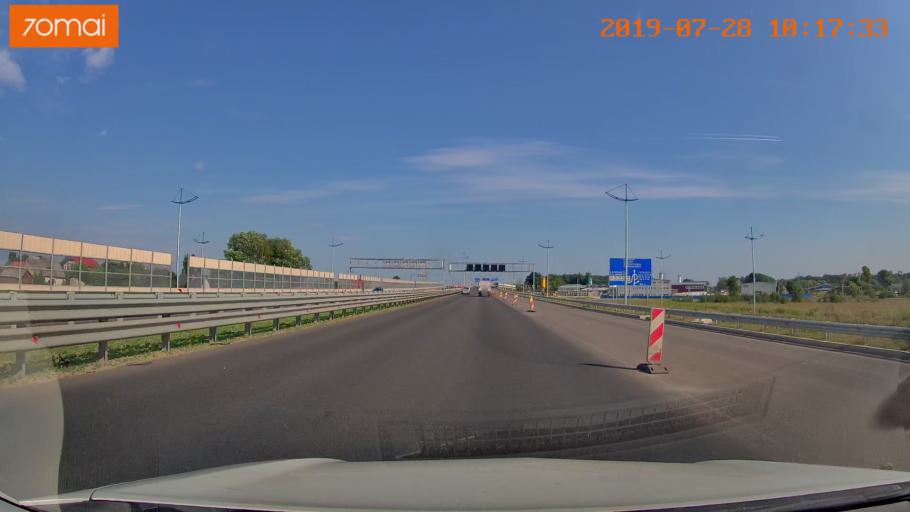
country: RU
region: Kaliningrad
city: Maloye Isakovo
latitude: 54.7411
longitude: 20.5938
